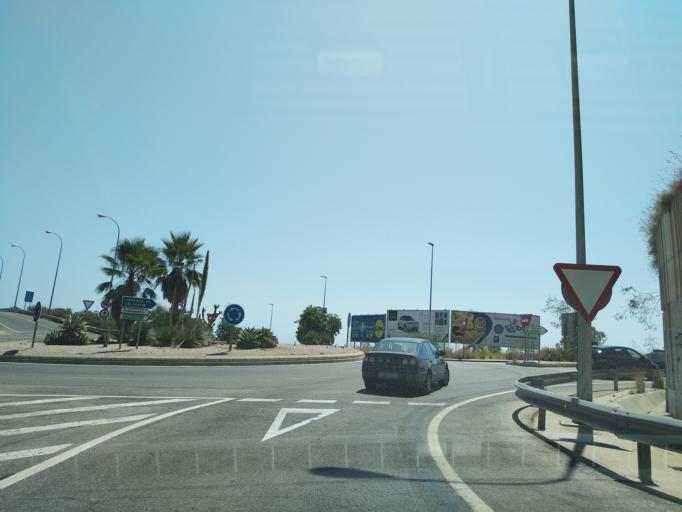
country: ES
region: Andalusia
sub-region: Provincia de Malaga
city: Malaga
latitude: 36.7334
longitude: -4.3769
